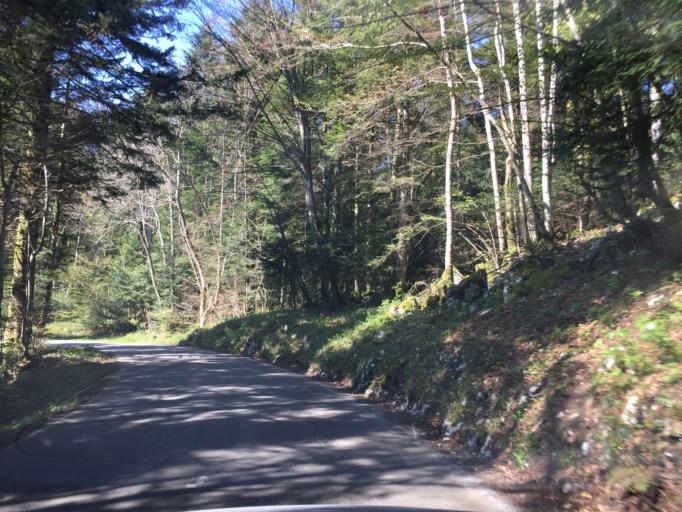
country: FR
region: Rhone-Alpes
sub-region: Departement de la Savoie
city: La Motte-Servolex
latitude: 45.5841
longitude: 5.8230
